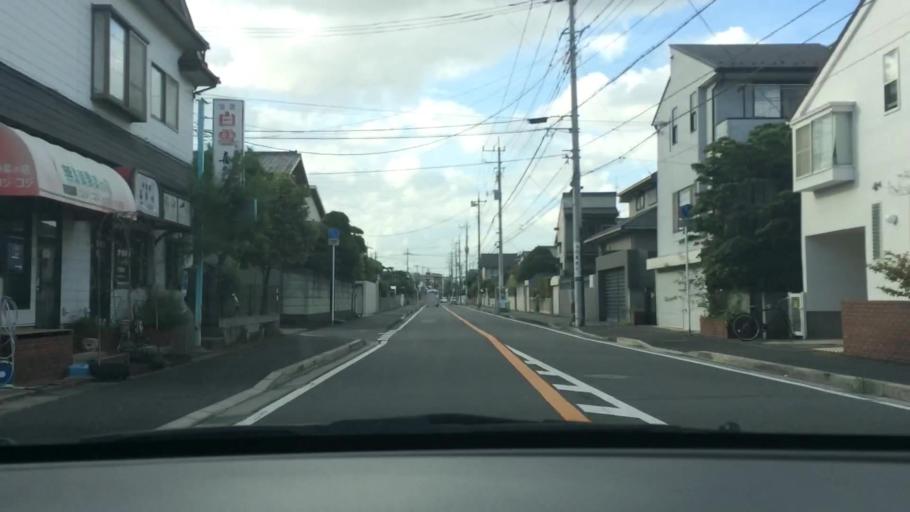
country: JP
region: Chiba
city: Nagareyama
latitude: 35.8955
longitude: 139.9089
